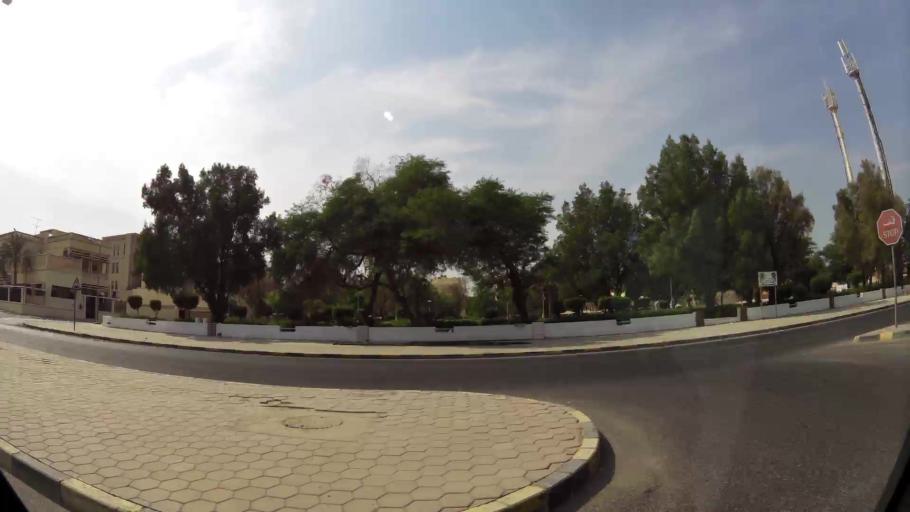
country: KW
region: Al Asimah
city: Ash Shamiyah
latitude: 29.3391
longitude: 47.9764
